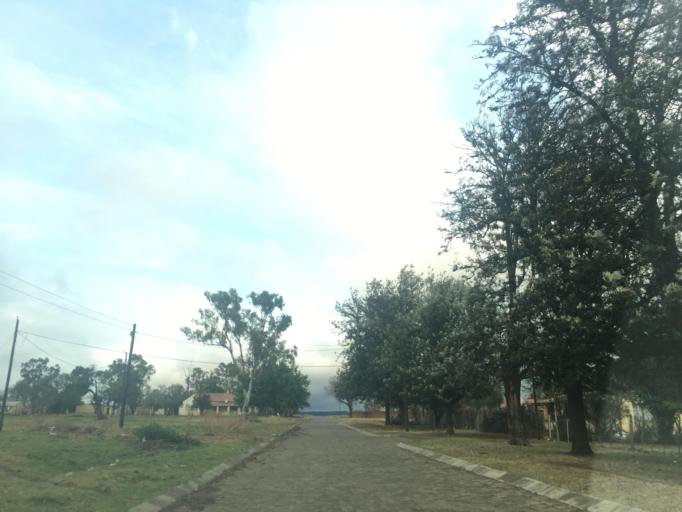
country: ZA
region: Eastern Cape
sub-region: Chris Hani District Municipality
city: Cala
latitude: -31.5245
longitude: 27.7011
